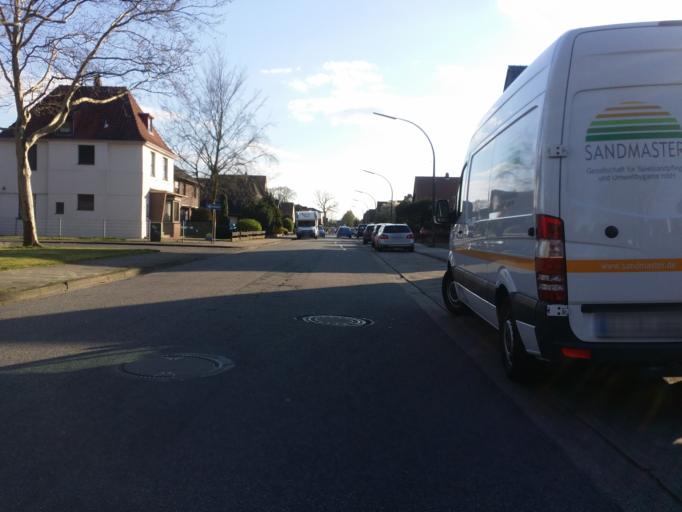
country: DE
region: Lower Saxony
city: Delmenhorst
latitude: 53.0269
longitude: 8.6258
